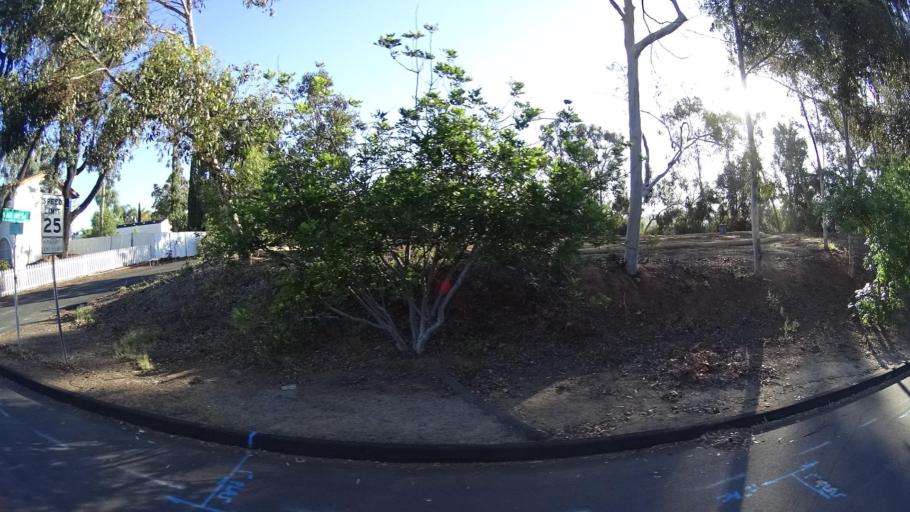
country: US
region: California
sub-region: San Diego County
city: Bonita
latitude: 32.6682
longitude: -117.0292
